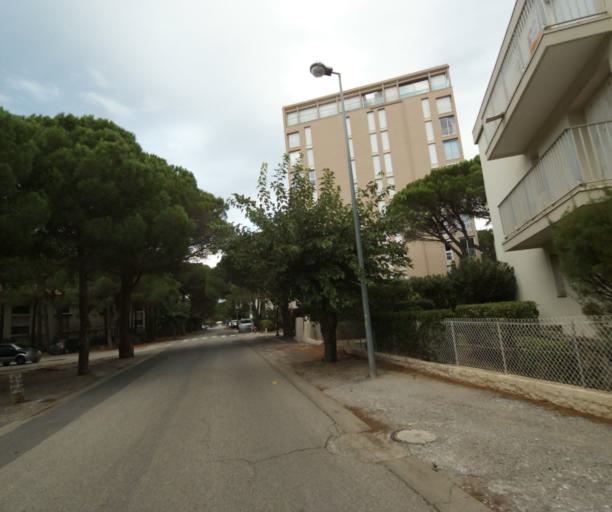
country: FR
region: Languedoc-Roussillon
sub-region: Departement des Pyrenees-Orientales
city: Argelers
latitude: 42.5628
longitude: 3.0451
